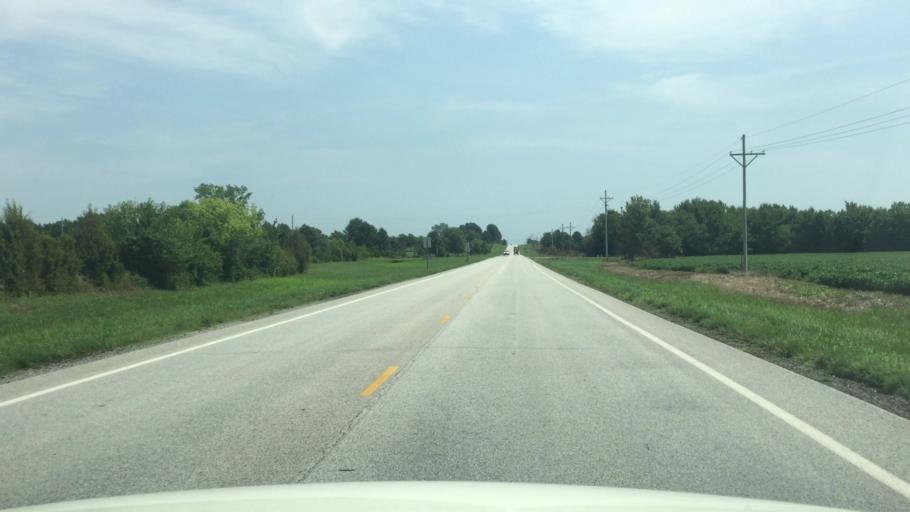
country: US
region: Kansas
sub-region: Cherokee County
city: Columbus
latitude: 37.1781
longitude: -94.7984
